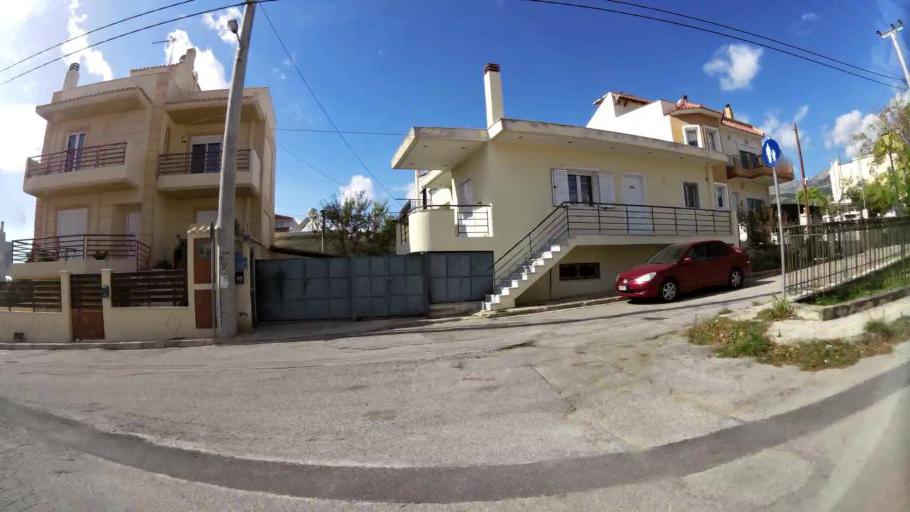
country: GR
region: Attica
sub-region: Nomarchia Anatolikis Attikis
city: Acharnes
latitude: 38.1072
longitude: 23.7393
